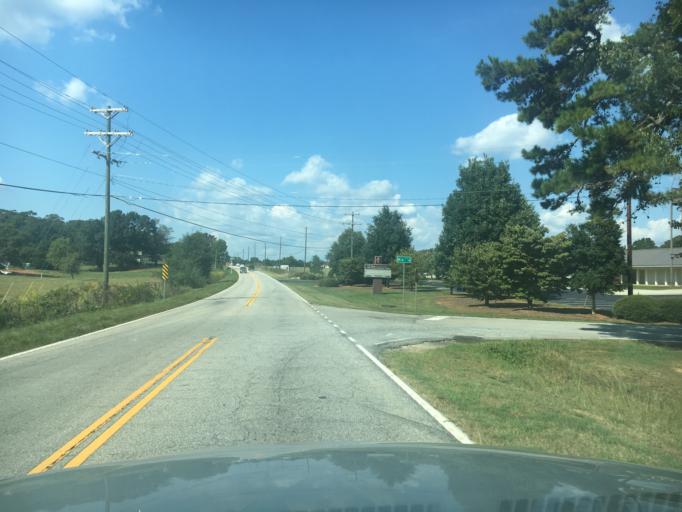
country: US
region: South Carolina
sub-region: Anderson County
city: Pendleton
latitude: 34.5667
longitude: -82.8072
